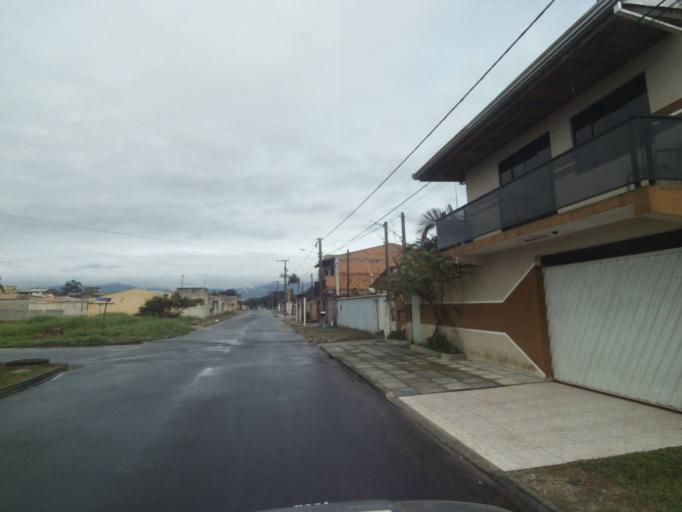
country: BR
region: Parana
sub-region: Paranagua
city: Paranagua
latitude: -25.5604
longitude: -48.5666
